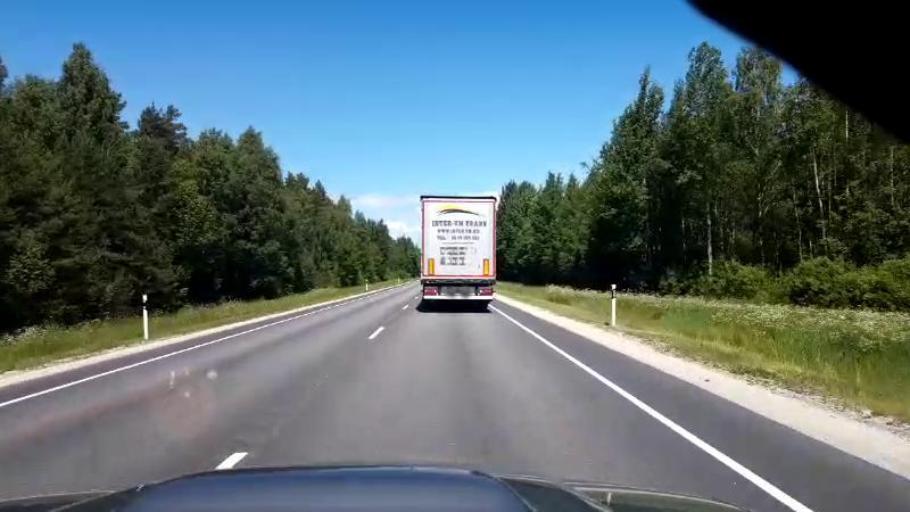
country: EE
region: Paernumaa
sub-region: Paernu linn
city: Parnu
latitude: 58.1176
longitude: 24.5106
